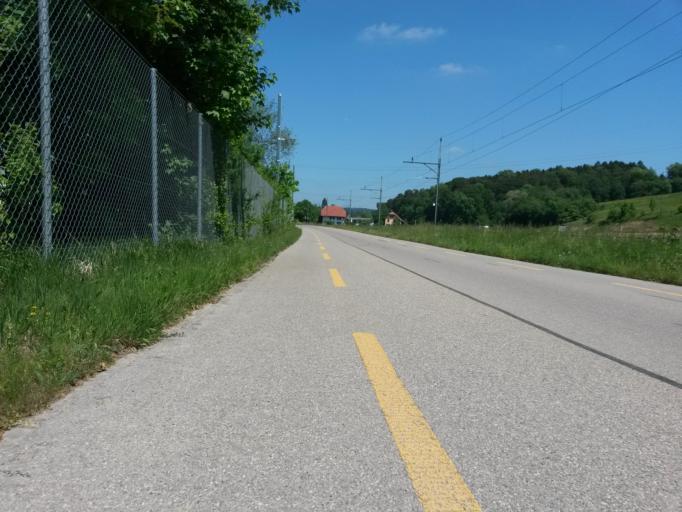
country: CH
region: Bern
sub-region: Seeland District
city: Aarberg
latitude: 47.0565
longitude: 7.2910
